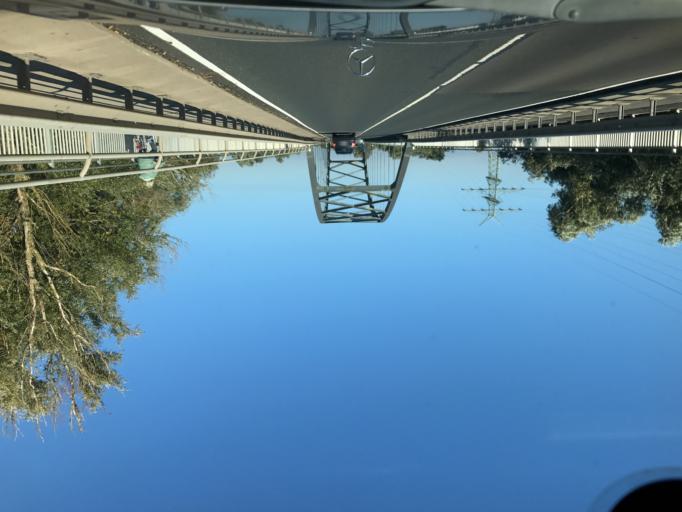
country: DE
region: Lower Saxony
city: Papenburg
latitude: 53.1022
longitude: 7.3528
